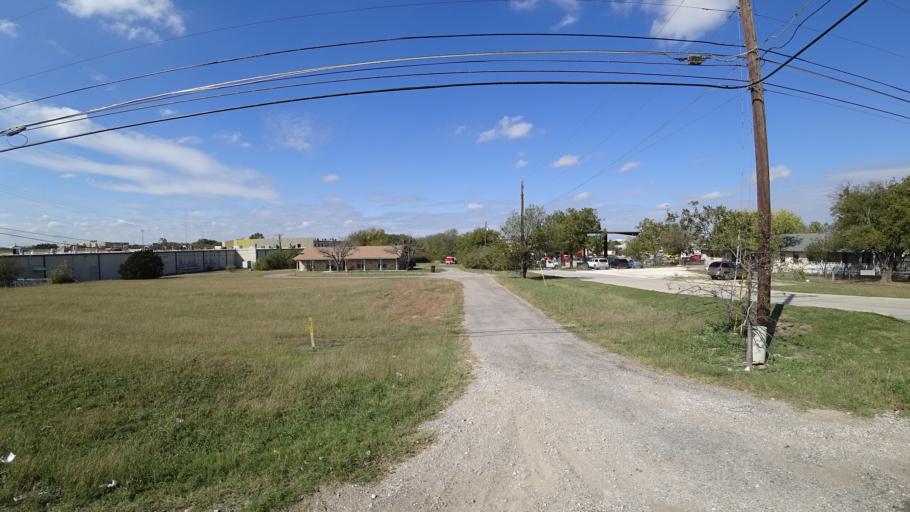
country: US
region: Texas
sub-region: Travis County
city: Windemere
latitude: 30.4507
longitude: -97.6550
